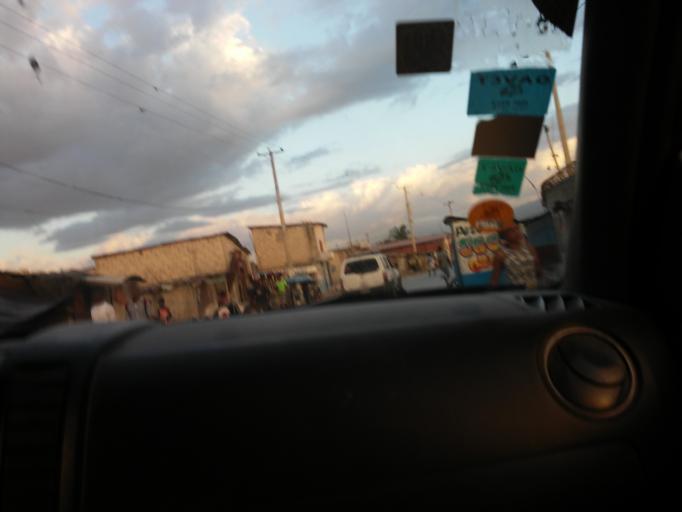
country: HT
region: Ouest
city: Port-au-Prince
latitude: 18.5652
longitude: -72.3466
